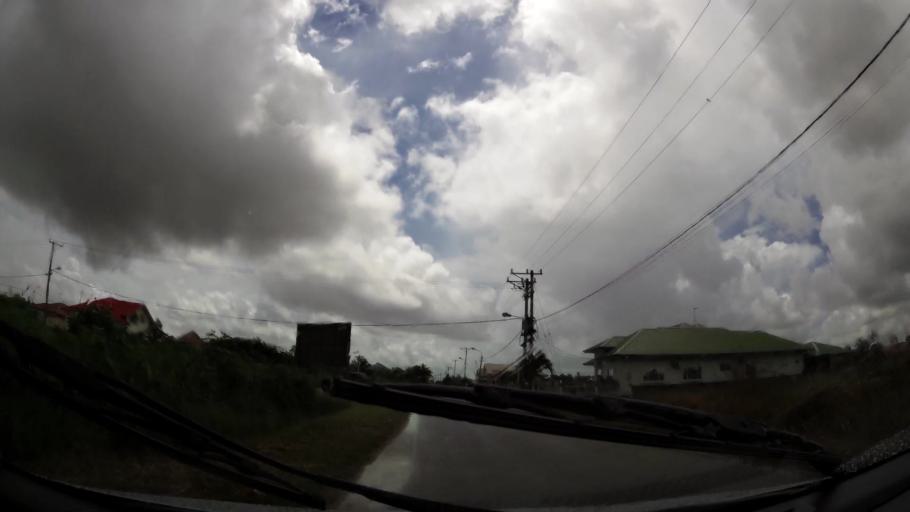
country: SR
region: Paramaribo
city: Paramaribo
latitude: 5.8290
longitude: -55.2334
